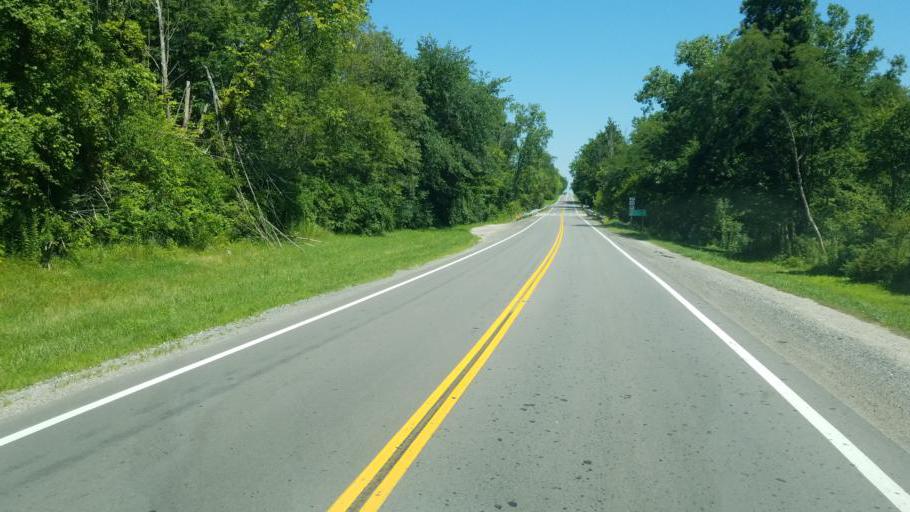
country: US
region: Ohio
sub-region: Marion County
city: Prospect
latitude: 40.4638
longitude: -83.0748
